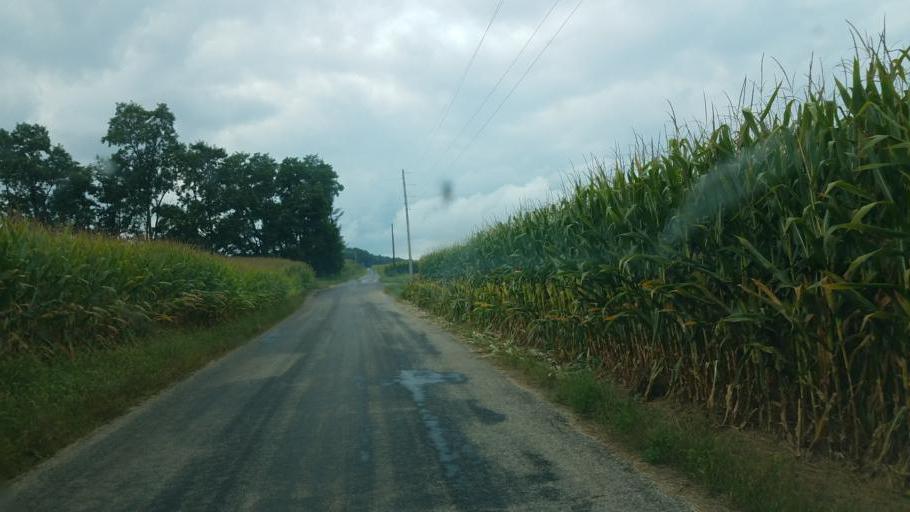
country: US
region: Ohio
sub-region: Ashland County
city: Loudonville
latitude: 40.6091
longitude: -82.3561
